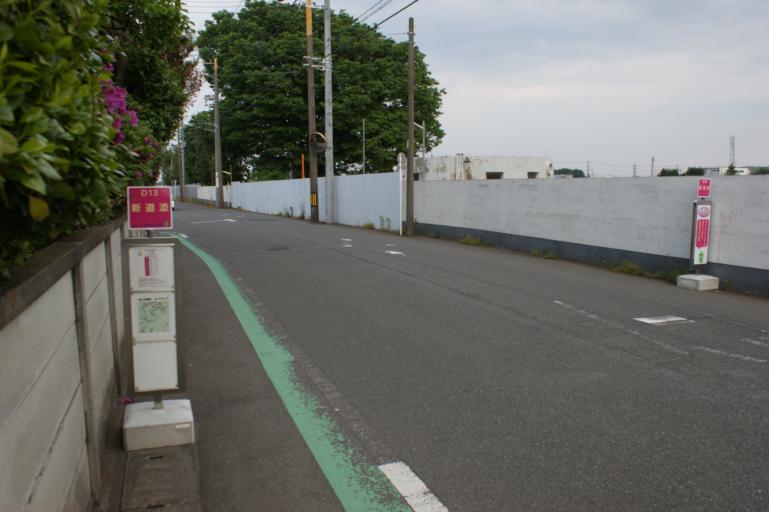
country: JP
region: Kanagawa
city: Minami-rinkan
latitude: 35.4536
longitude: 139.4726
